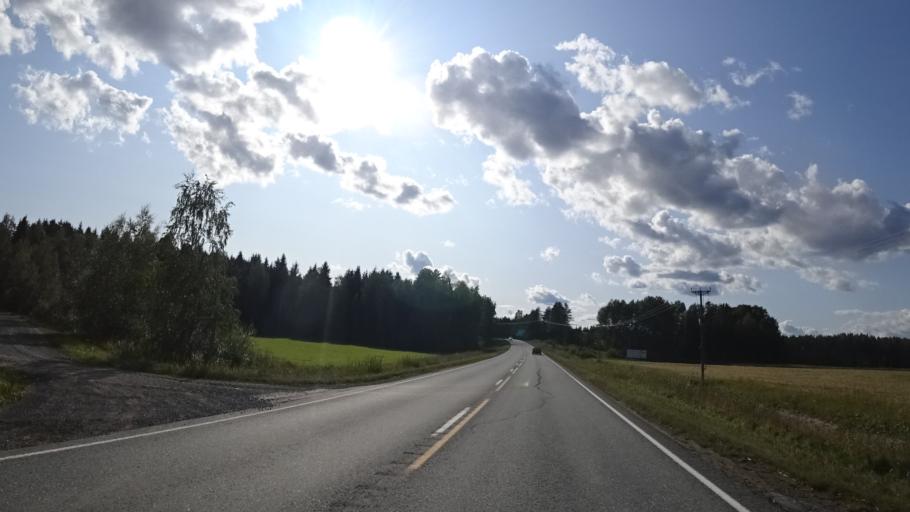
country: FI
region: North Karelia
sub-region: Keski-Karjala
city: Kitee
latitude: 62.0901
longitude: 30.0187
